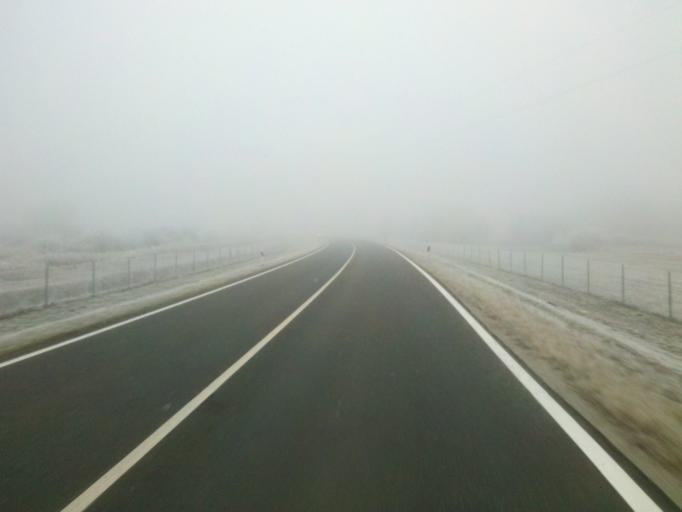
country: HR
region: Varazdinska
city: Jalkovec
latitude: 46.2686
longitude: 16.3426
